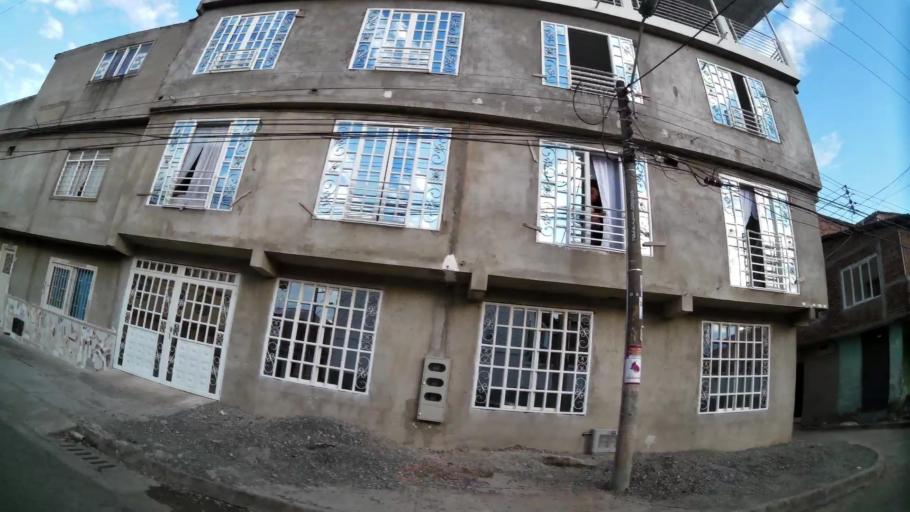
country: CO
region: Valle del Cauca
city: Cali
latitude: 3.4258
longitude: -76.5069
